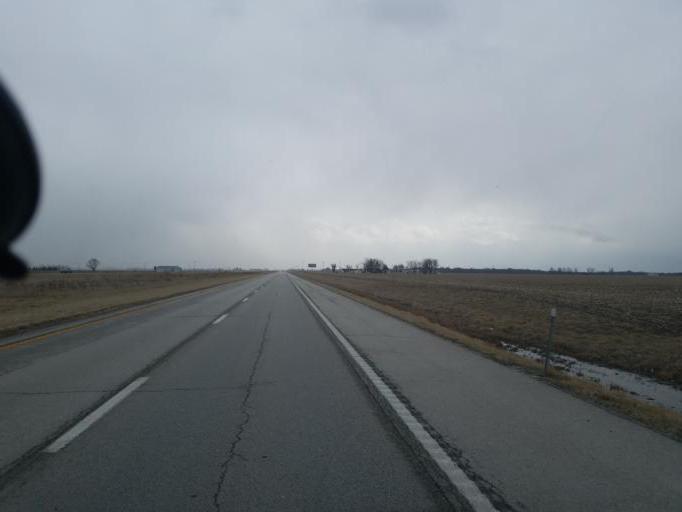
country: US
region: Missouri
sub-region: Randolph County
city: Huntsville
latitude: 39.5677
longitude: -92.4631
